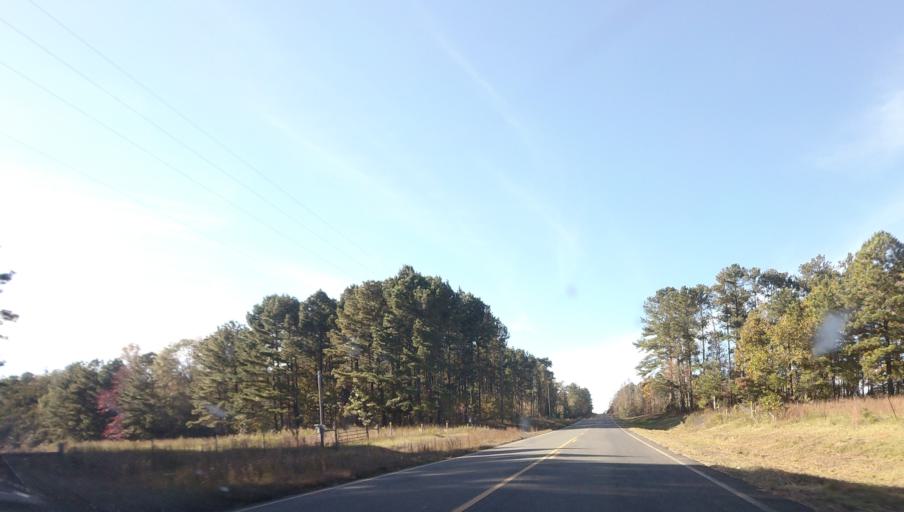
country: US
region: Georgia
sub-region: Talbot County
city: Talbotton
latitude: 32.6766
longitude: -84.6374
